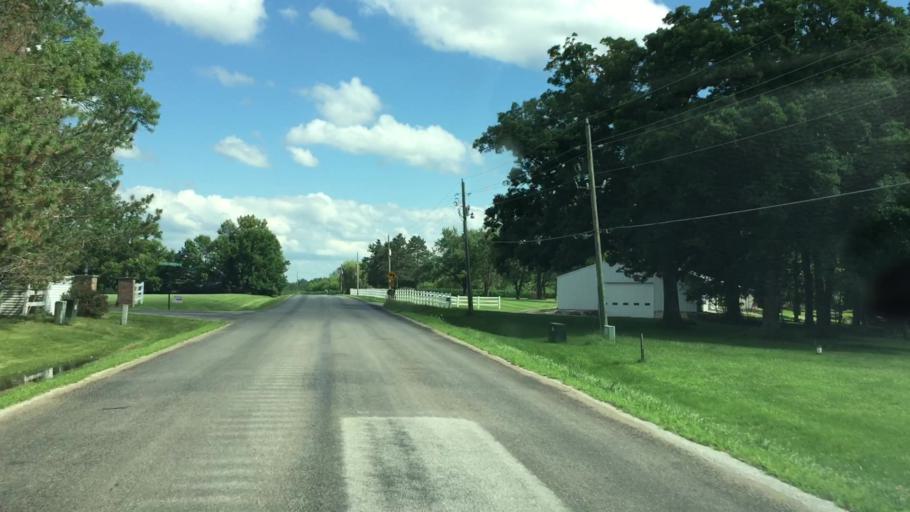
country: US
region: Iowa
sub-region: Linn County
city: Ely
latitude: 41.8187
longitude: -91.6214
